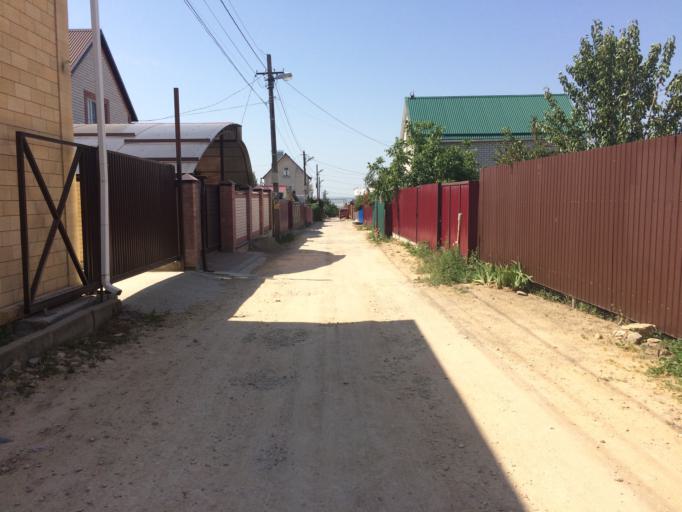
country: RU
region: Stavropol'skiy
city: Tatarka
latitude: 44.9861
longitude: 41.9421
